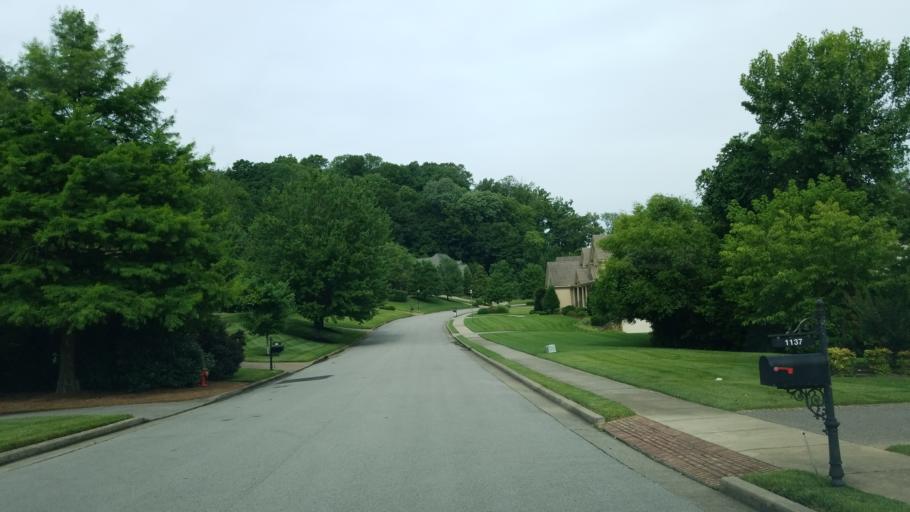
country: US
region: Tennessee
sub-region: Williamson County
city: Brentwood
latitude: 36.0547
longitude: -86.8093
